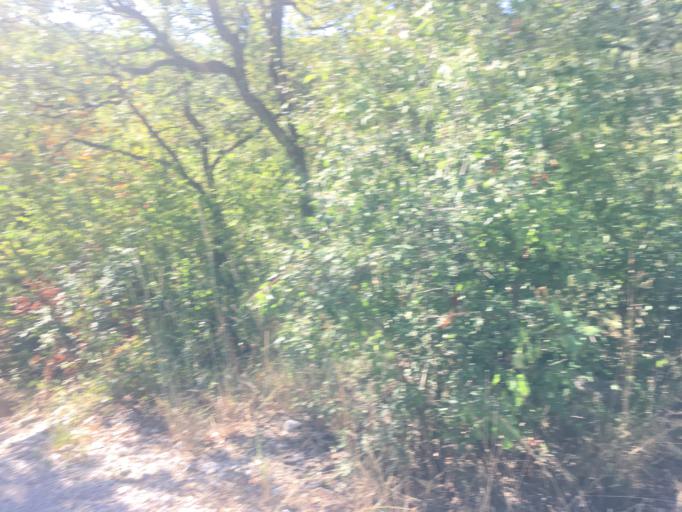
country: XK
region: Pristina
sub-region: Komuna e Prishtines
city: Pristina
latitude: 42.6659
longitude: 21.2226
